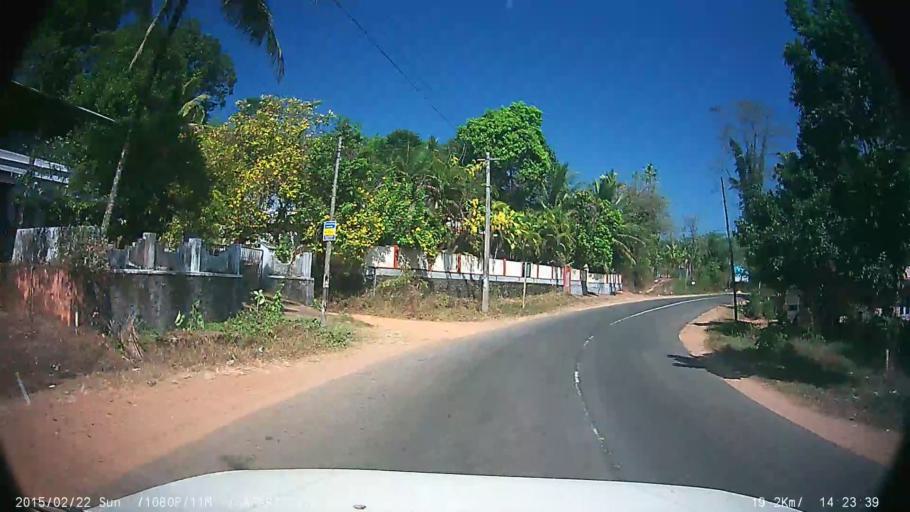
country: IN
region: Kerala
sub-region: Kottayam
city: Lalam
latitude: 9.5679
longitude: 76.7112
